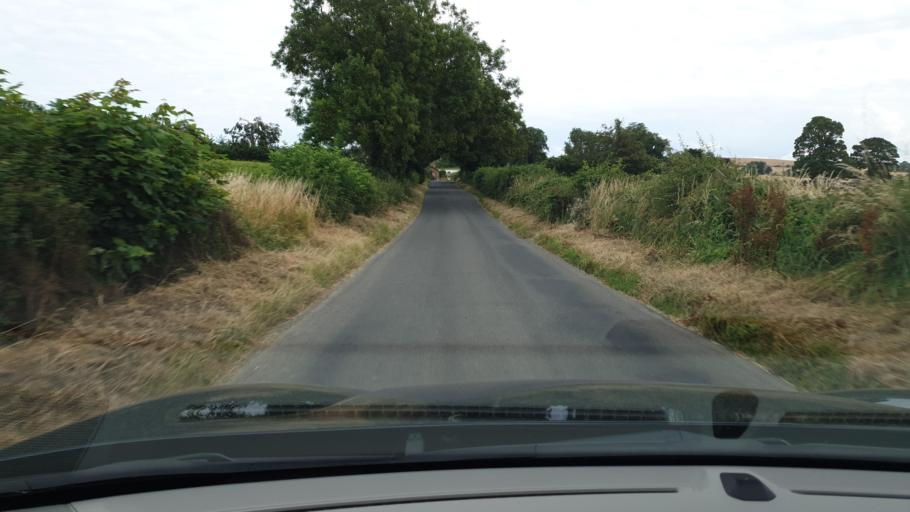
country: IE
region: Leinster
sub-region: An Mhi
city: Stamullin
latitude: 53.5827
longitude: -6.3090
